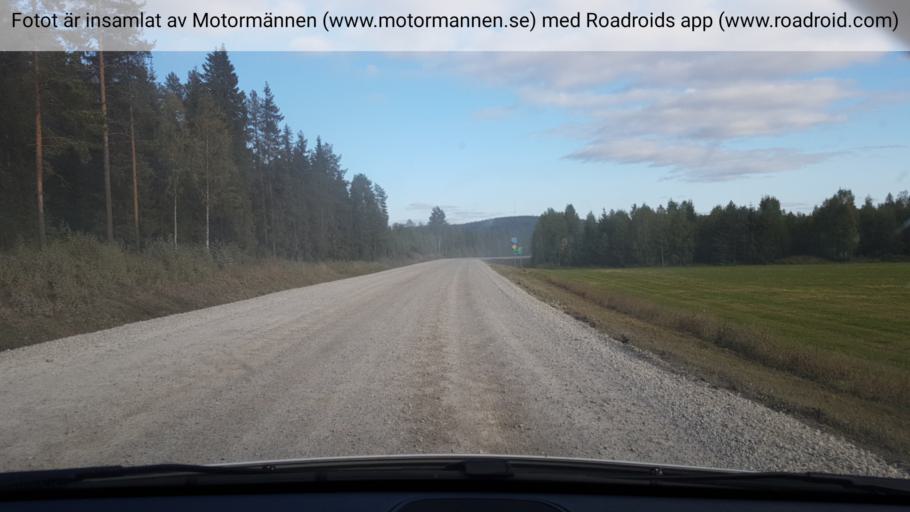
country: SE
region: Vaesterbotten
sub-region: Vindelns Kommun
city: Vindeln
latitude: 64.0532
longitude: 19.6667
